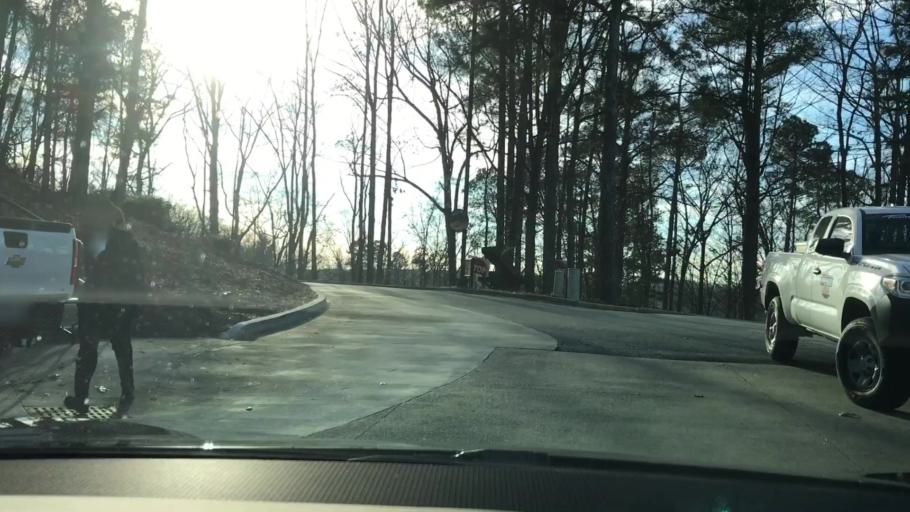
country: US
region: Georgia
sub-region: Gwinnett County
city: Buford
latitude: 34.1874
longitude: -84.0175
